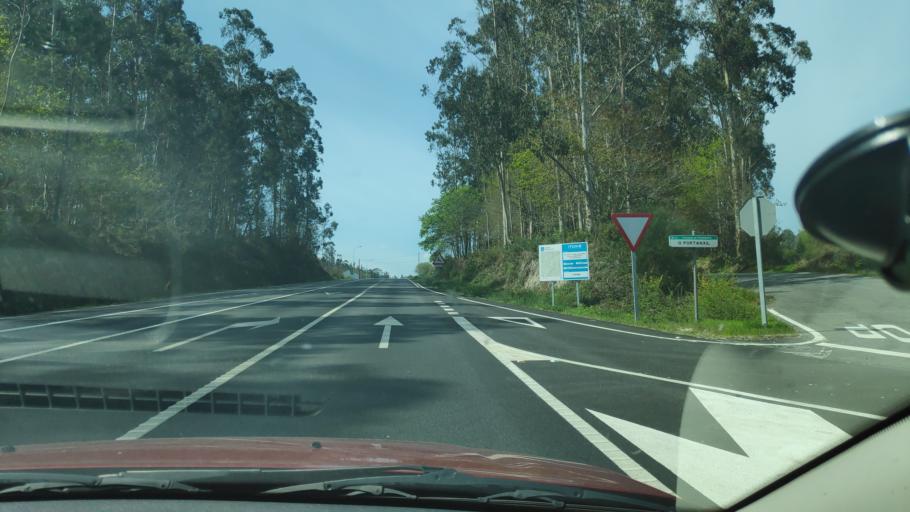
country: ES
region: Galicia
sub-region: Provincia da Coruna
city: Ames
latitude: 42.8786
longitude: -8.6762
